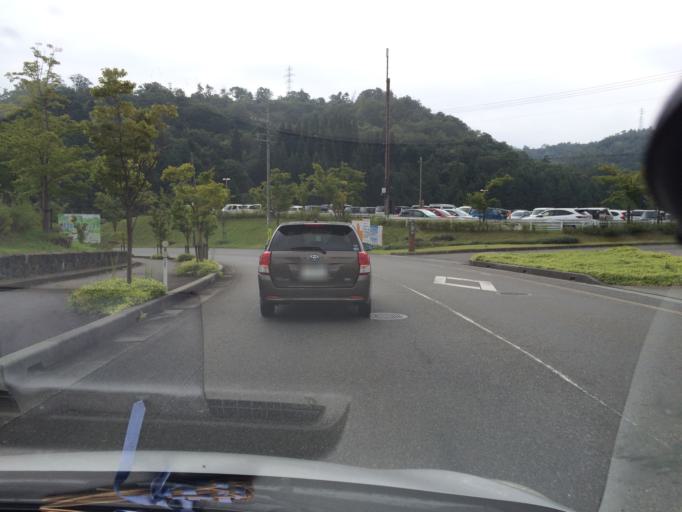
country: JP
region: Hyogo
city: Toyooka
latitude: 35.5256
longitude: 134.8061
